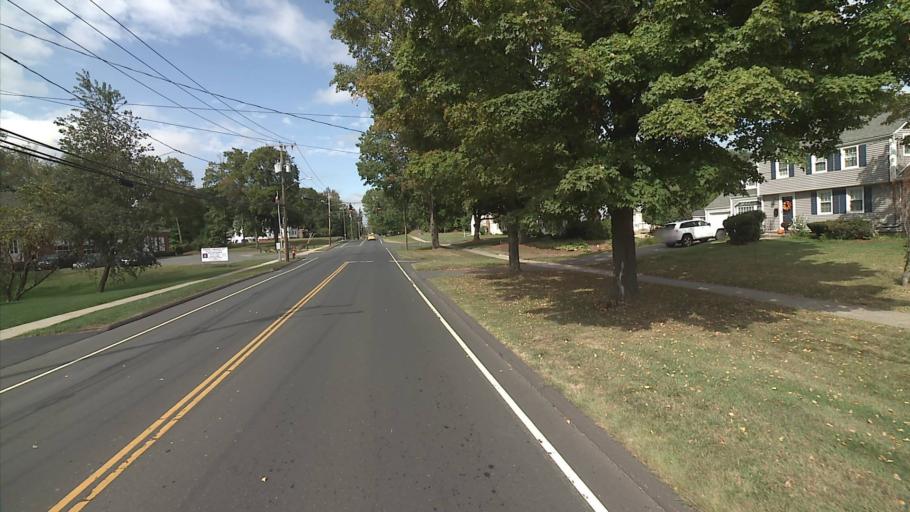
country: US
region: Connecticut
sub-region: Hartford County
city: Newington
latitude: 41.6911
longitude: -72.7219
